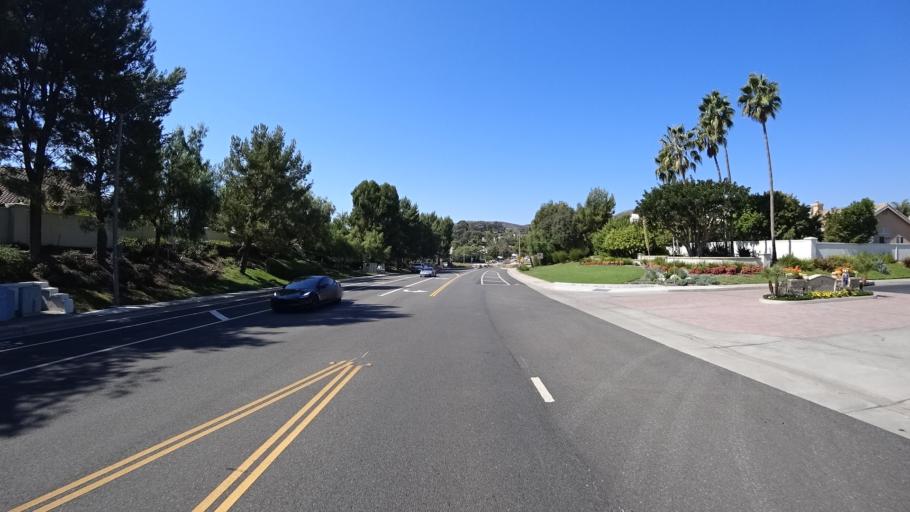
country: US
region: California
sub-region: Orange County
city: San Juan Capistrano
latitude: 33.4737
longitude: -117.6270
